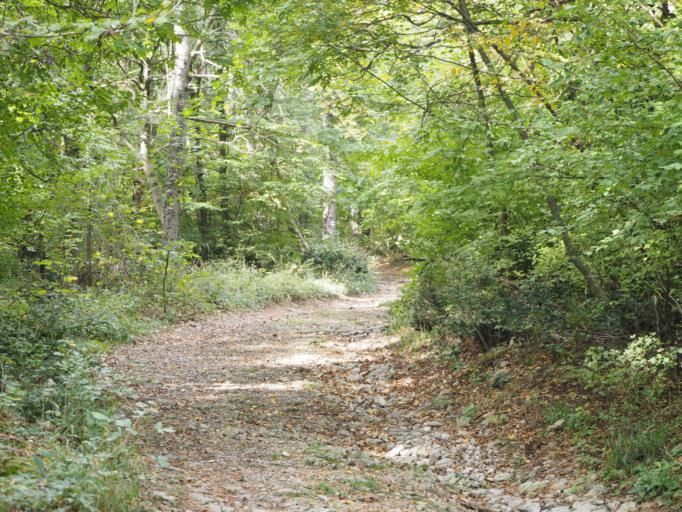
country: HU
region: Baranya
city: Pecs
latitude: 46.1125
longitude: 18.1799
